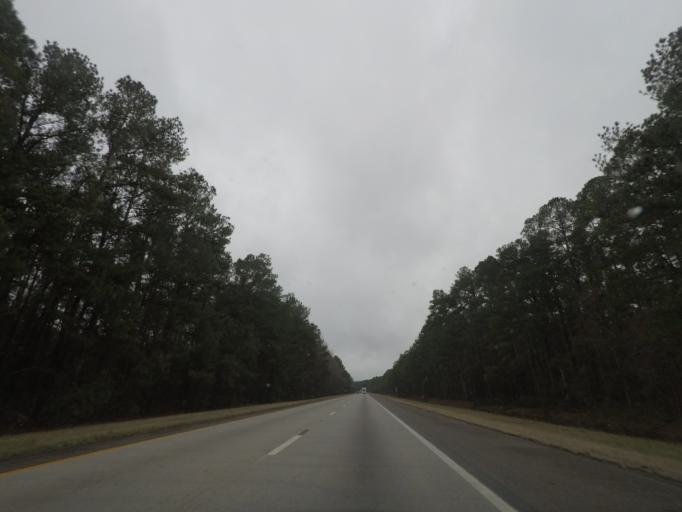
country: US
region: South Carolina
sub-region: Colleton County
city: Walterboro
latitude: 33.0533
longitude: -80.6671
